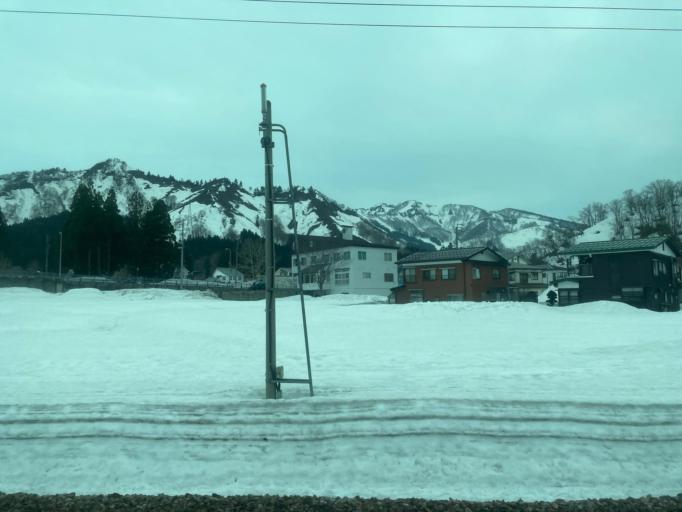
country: JP
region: Niigata
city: Shiozawa
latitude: 36.9256
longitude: 138.8260
